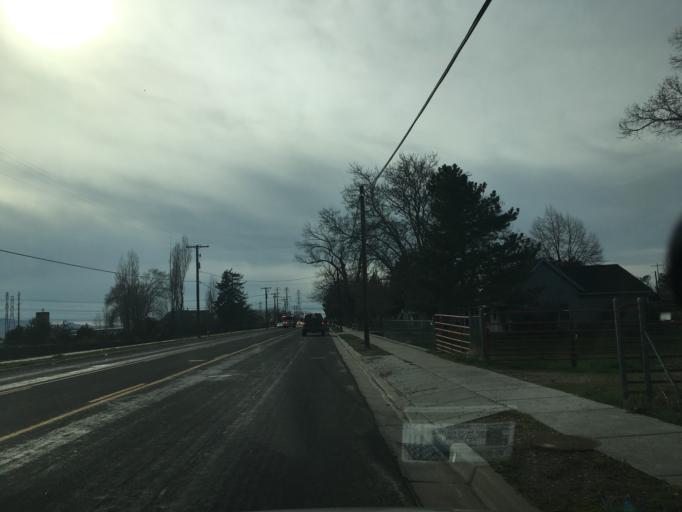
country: US
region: Utah
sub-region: Davis County
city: Layton
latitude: 41.0602
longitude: -112.0026
